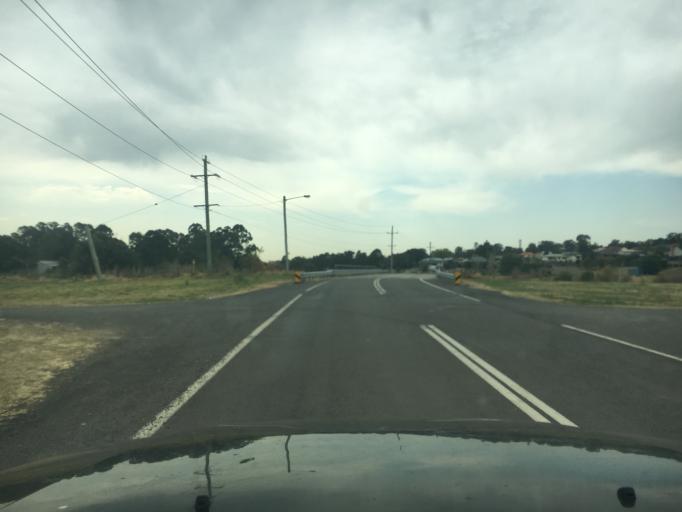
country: AU
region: New South Wales
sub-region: Maitland Municipality
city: East Maitland
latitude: -32.7512
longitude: 151.5719
